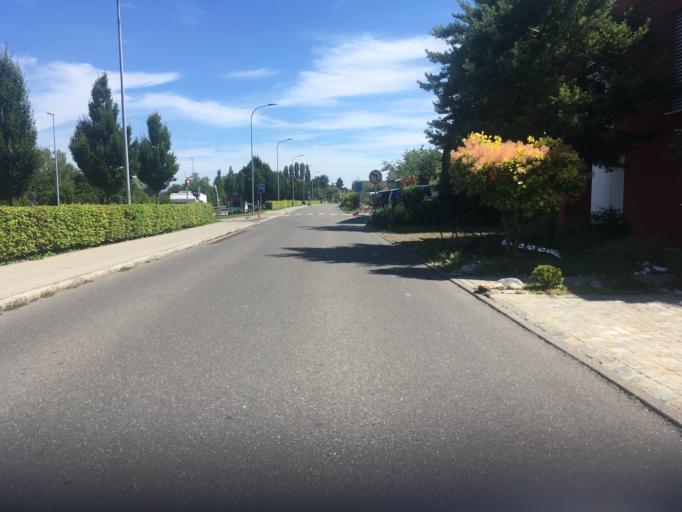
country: CH
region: Fribourg
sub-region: See District
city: Murten
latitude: 46.9320
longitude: 7.1195
